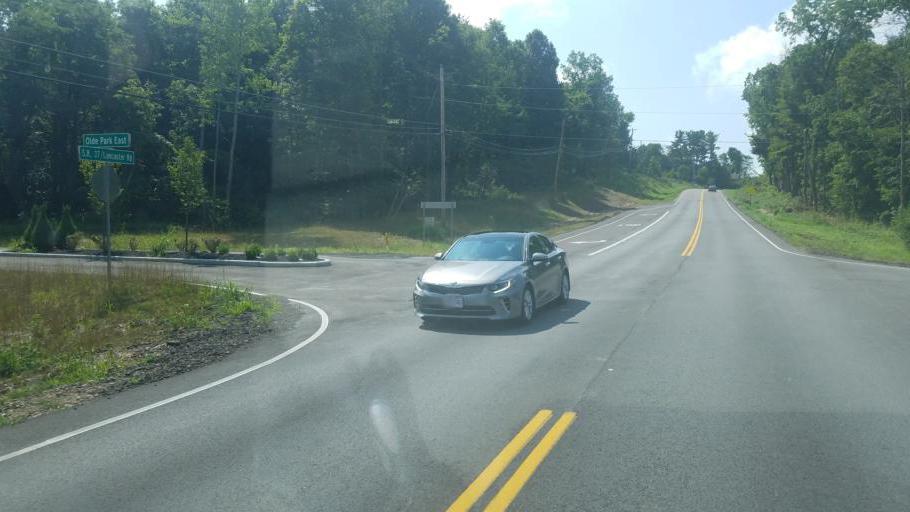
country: US
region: Ohio
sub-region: Licking County
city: Granville South
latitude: 40.0453
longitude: -82.5228
